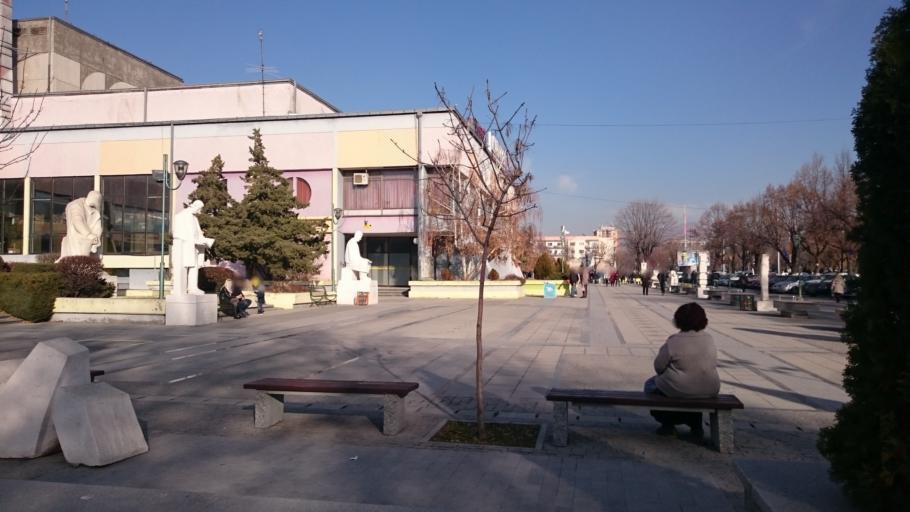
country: MK
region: Prilep
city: Prilep
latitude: 41.3450
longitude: 21.5505
